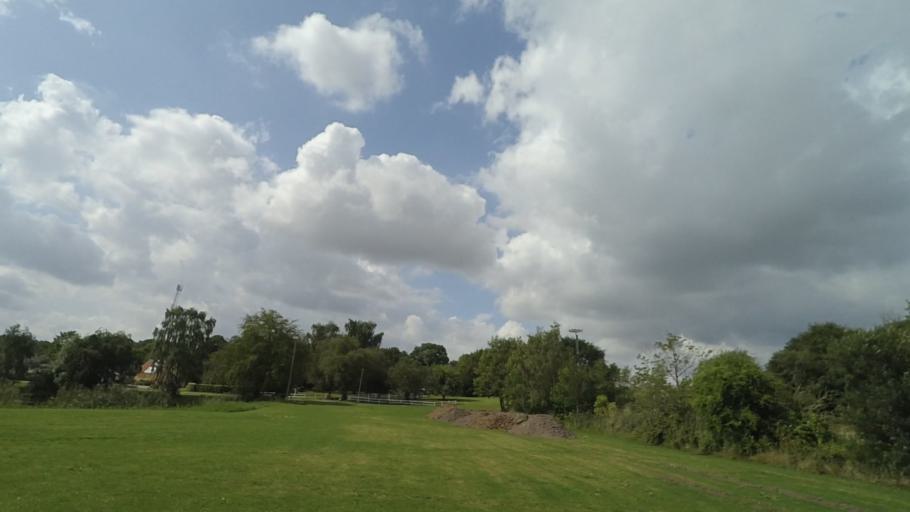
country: DK
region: Central Jutland
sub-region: Norddjurs Kommune
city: Allingabro
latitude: 56.5401
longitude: 10.3637
